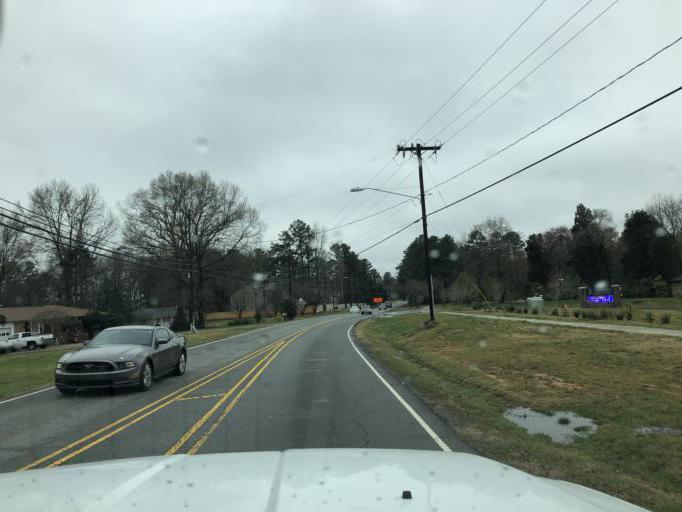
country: US
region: North Carolina
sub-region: Gaston County
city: Mount Holly
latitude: 35.3193
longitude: -80.9541
